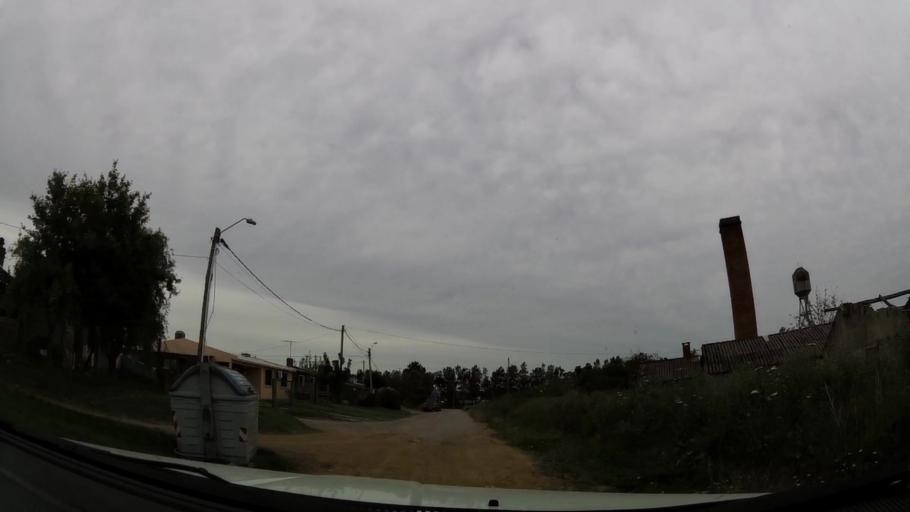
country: UY
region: Maldonado
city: Maldonado
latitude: -34.8812
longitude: -54.9825
